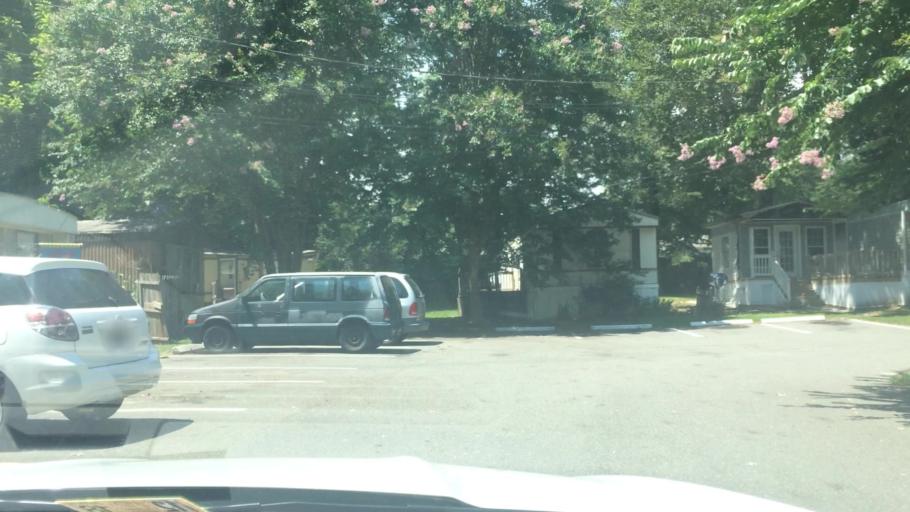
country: US
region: Virginia
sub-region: City of Williamsburg
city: Williamsburg
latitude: 37.2151
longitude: -76.6180
